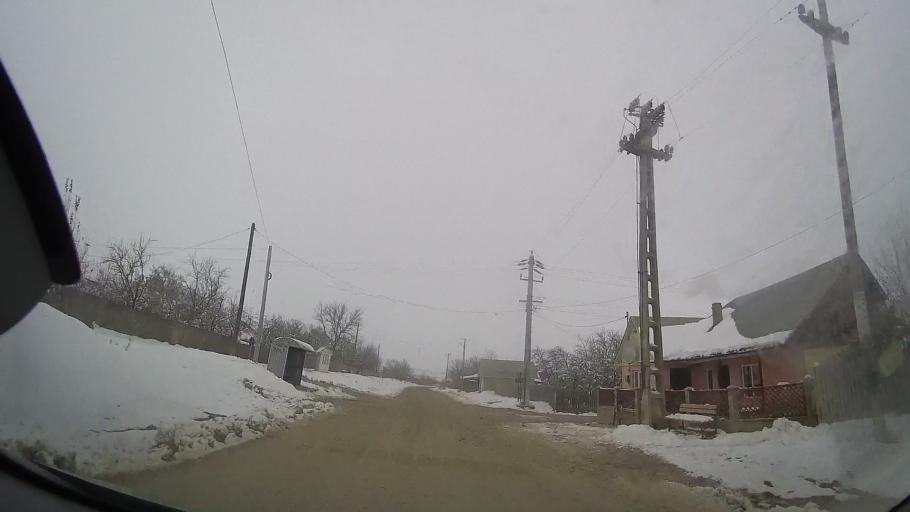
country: RO
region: Vaslui
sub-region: Comuna Todiresti
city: Todiresti
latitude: 46.8785
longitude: 27.3737
